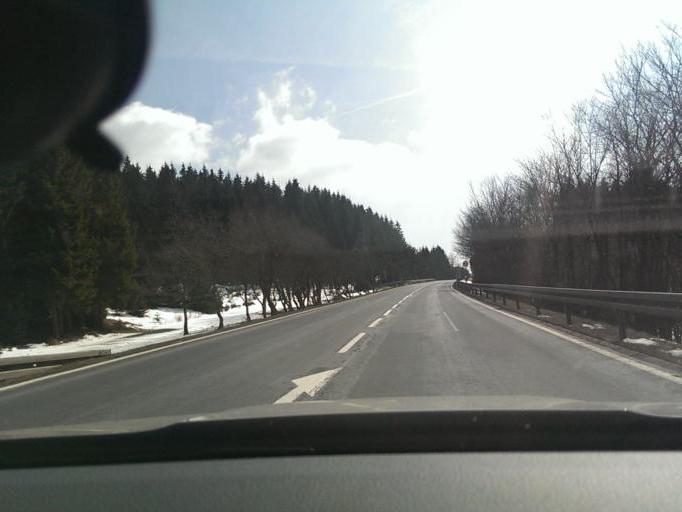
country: DE
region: Thuringia
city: Oberhof
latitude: 50.7090
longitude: 10.7336
